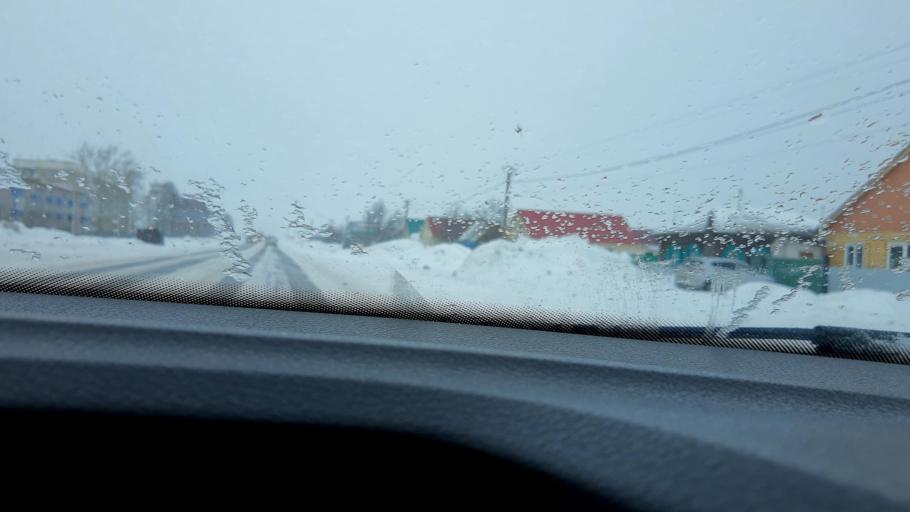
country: RU
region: Bashkortostan
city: Zirgan
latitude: 53.2312
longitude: 55.9161
